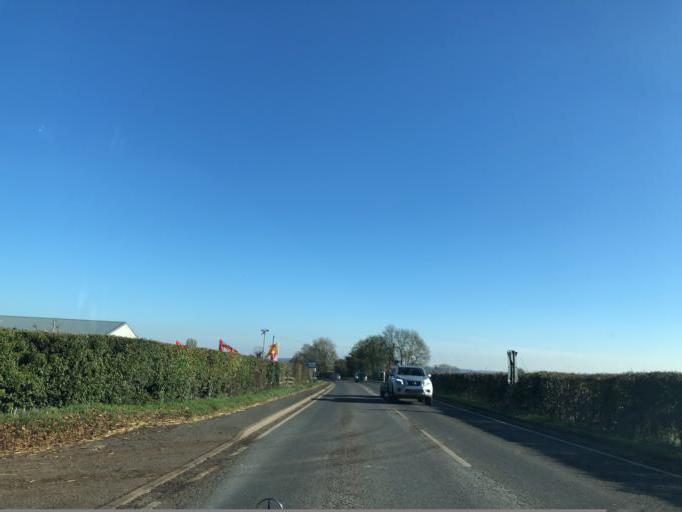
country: GB
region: England
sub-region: Warwickshire
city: Harbury
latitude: 52.2553
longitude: -1.4413
